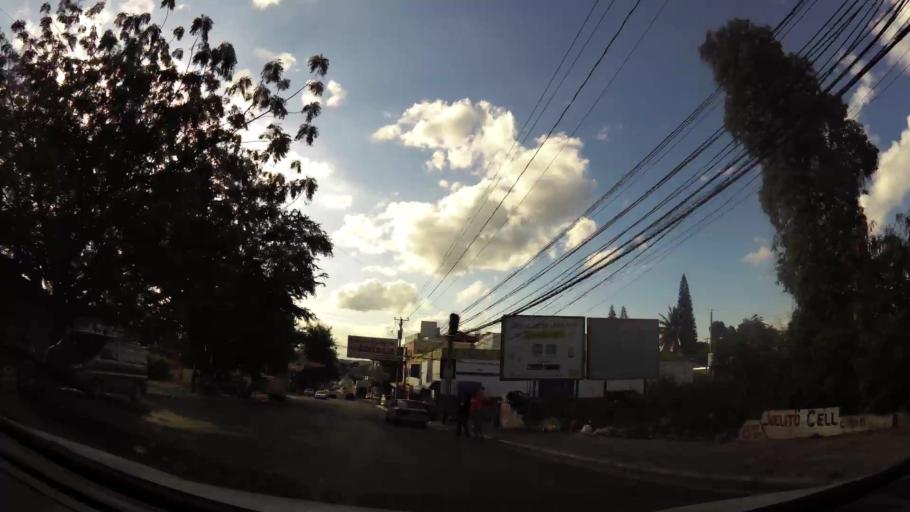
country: DO
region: Santiago
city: Santiago de los Caballeros
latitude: 19.4609
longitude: -70.7027
